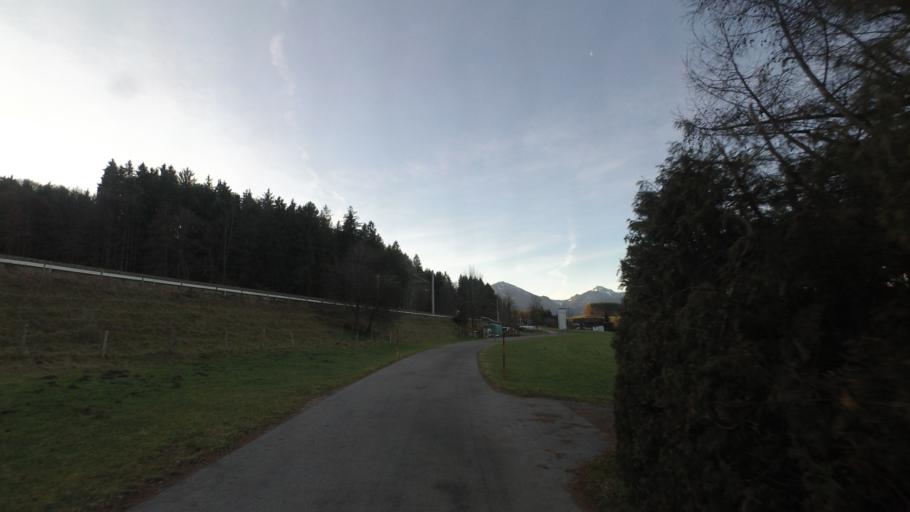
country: DE
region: Bavaria
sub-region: Upper Bavaria
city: Vachendorf
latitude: 47.8360
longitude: 12.6047
